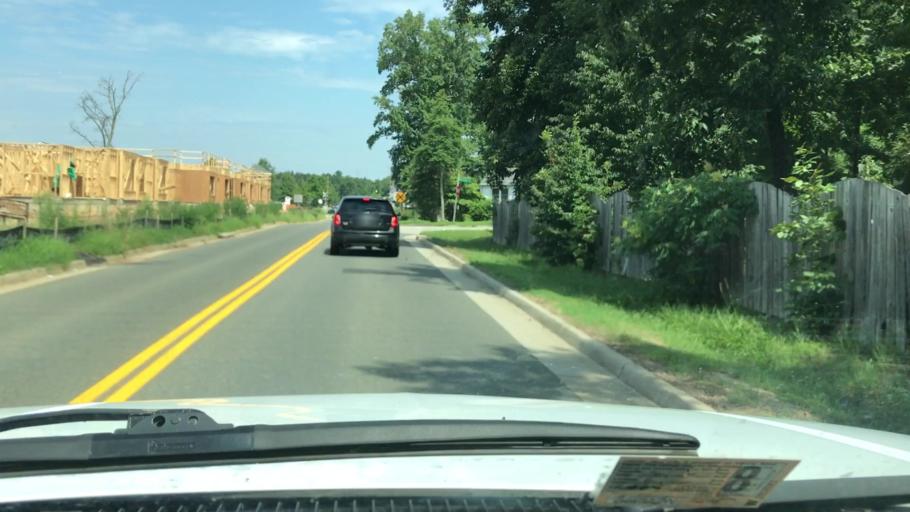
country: US
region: Virginia
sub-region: Chesterfield County
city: Brandermill
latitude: 37.5086
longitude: -77.6628
